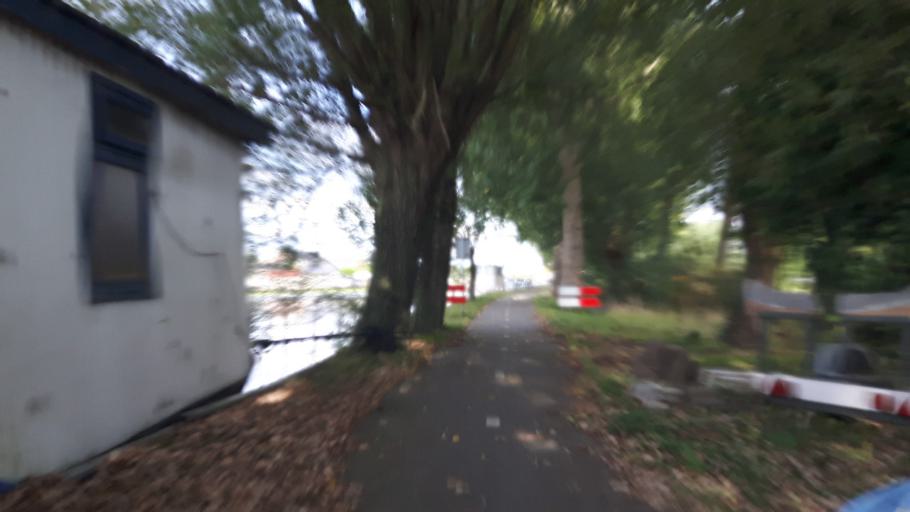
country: NL
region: South Holland
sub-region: Bodegraven-Reeuwijk
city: Bodegraven
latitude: 52.0924
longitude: 4.7390
